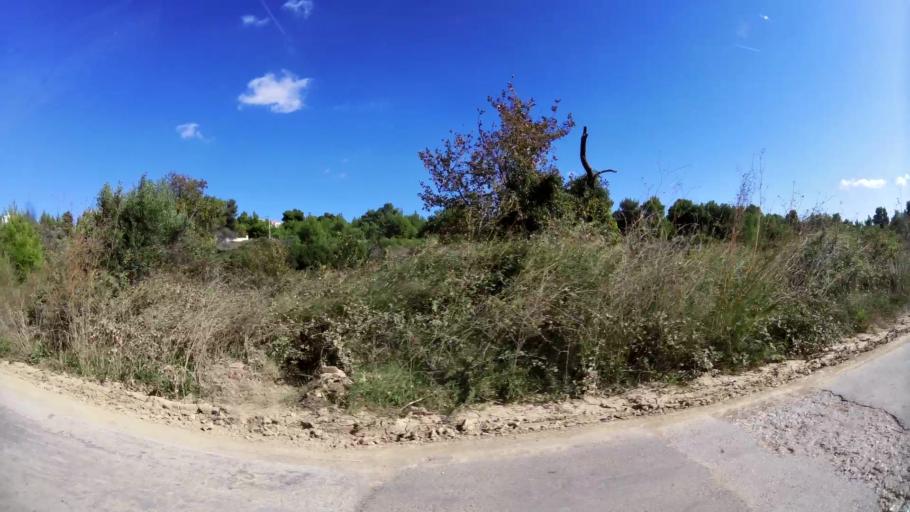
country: GR
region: Attica
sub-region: Nomarchia Anatolikis Attikis
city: Dioni
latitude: 38.0194
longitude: 23.9271
